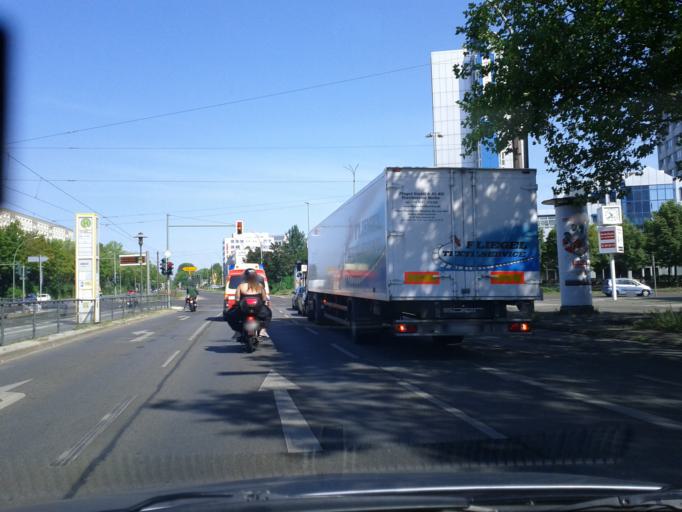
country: DE
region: Berlin
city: Fennpfuhl
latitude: 52.5327
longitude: 13.4767
